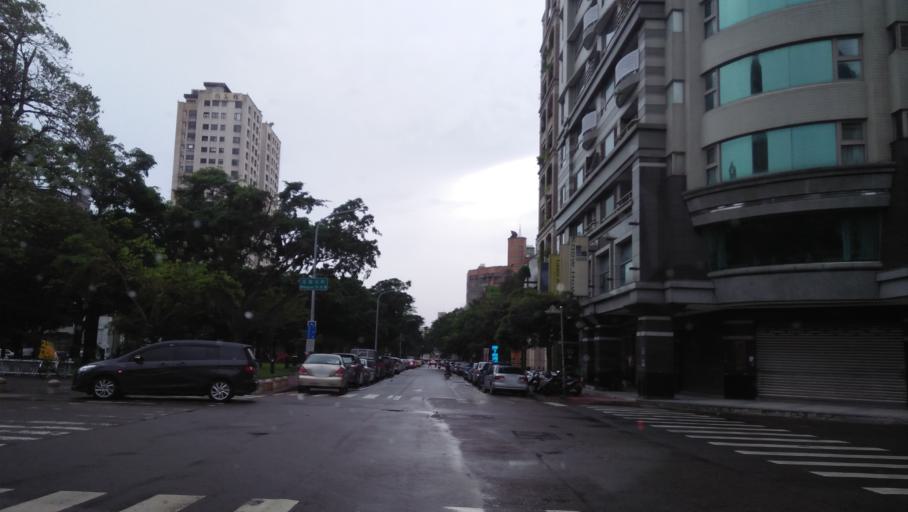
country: TW
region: Taiwan
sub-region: Taichung City
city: Taichung
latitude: 24.1354
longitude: 120.6626
